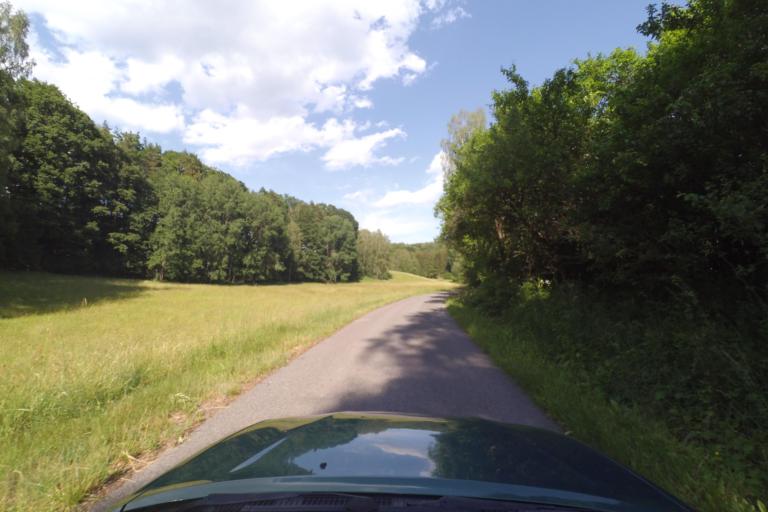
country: CZ
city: Osecna
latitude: 50.6714
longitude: 14.8803
